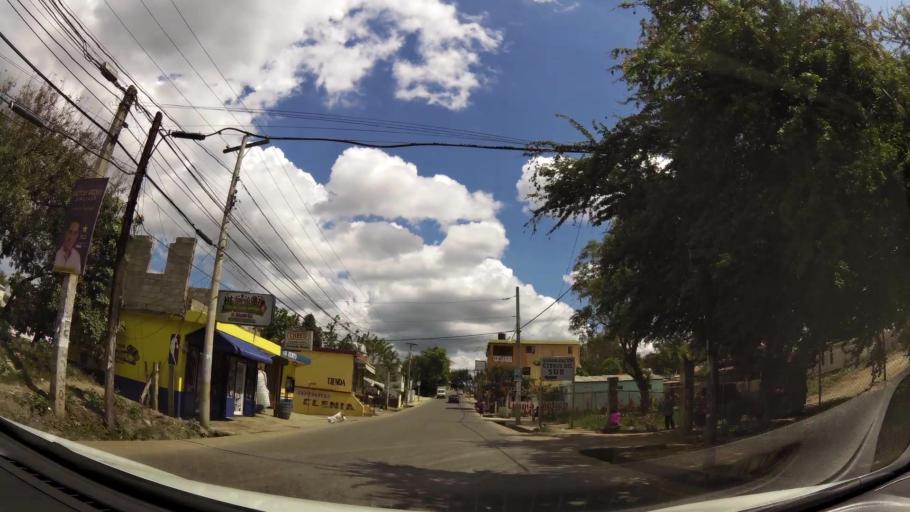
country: DO
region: Santiago
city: Santiago de los Caballeros
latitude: 19.4109
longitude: -70.6733
